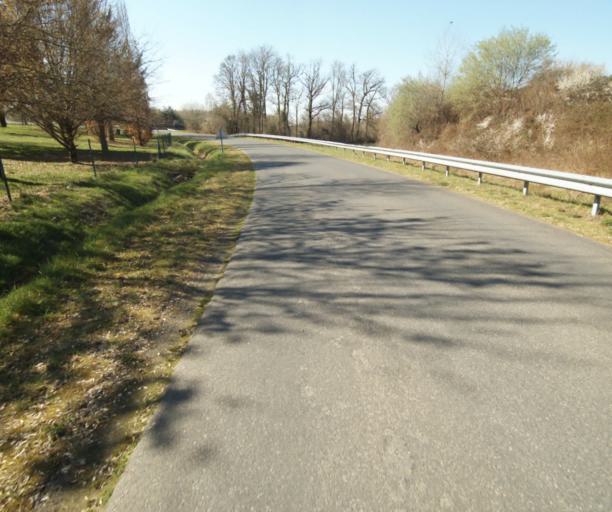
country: FR
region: Limousin
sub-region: Departement de la Correze
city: Saint-Mexant
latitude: 45.2843
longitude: 1.6198
